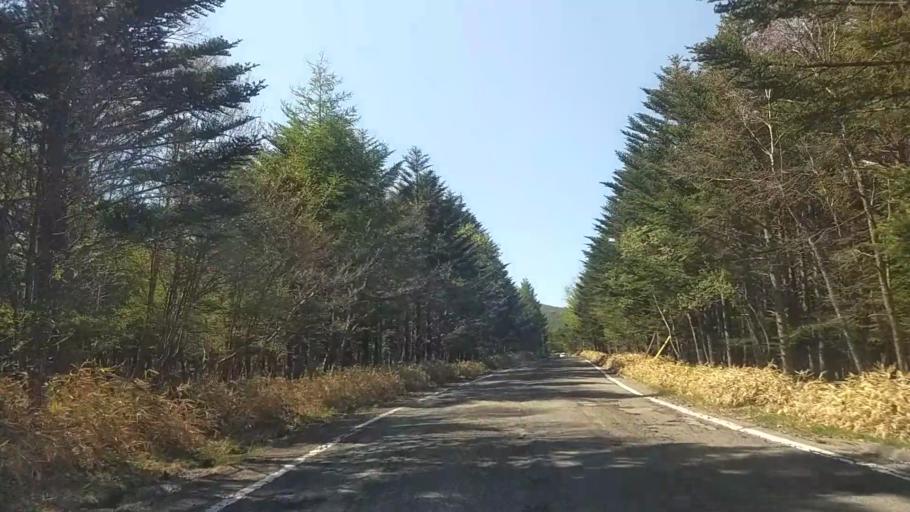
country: JP
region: Yamanashi
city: Nirasaki
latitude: 35.9459
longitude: 138.4192
